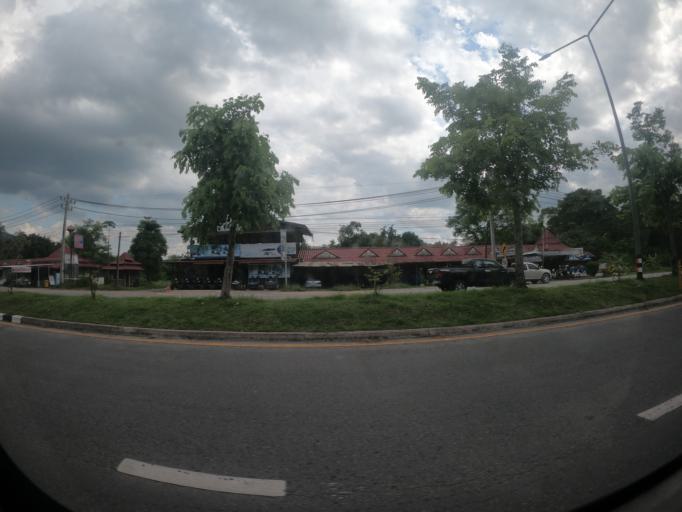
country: TH
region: Nakhon Nayok
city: Nakhon Nayok
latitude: 14.3150
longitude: 101.3138
